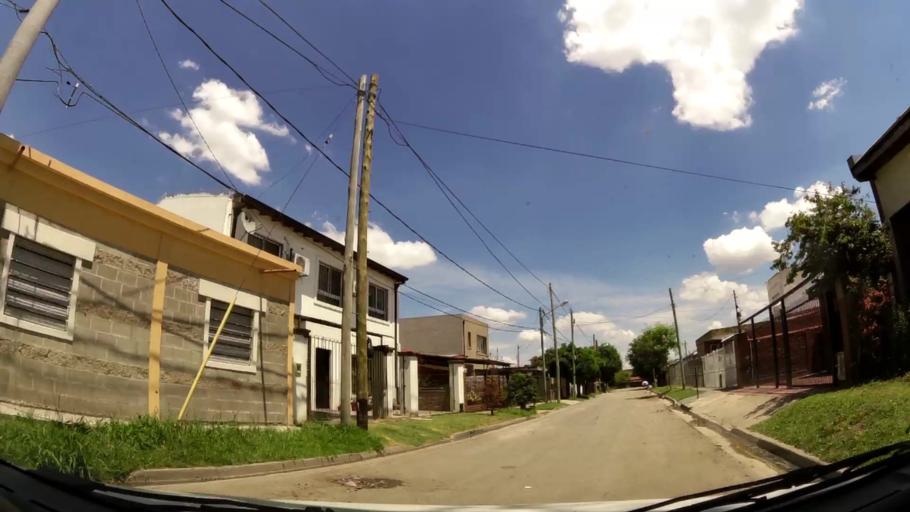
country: AR
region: Buenos Aires
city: Ituzaingo
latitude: -34.6585
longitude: -58.6900
